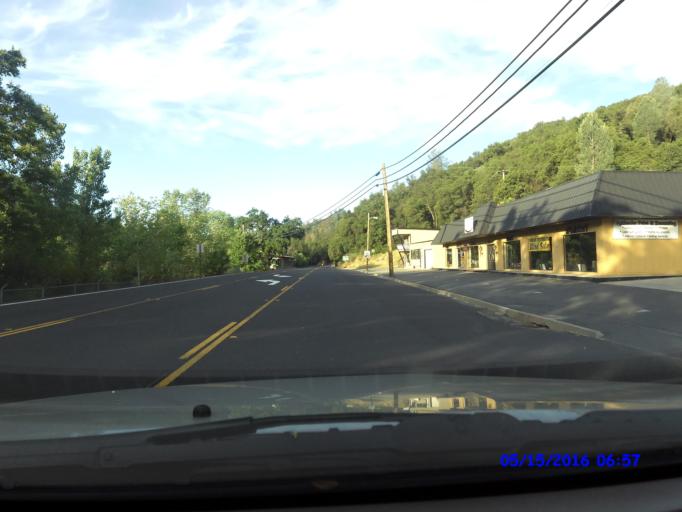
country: US
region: California
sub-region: Tuolumne County
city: Sonora
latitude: 37.9764
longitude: -120.3921
